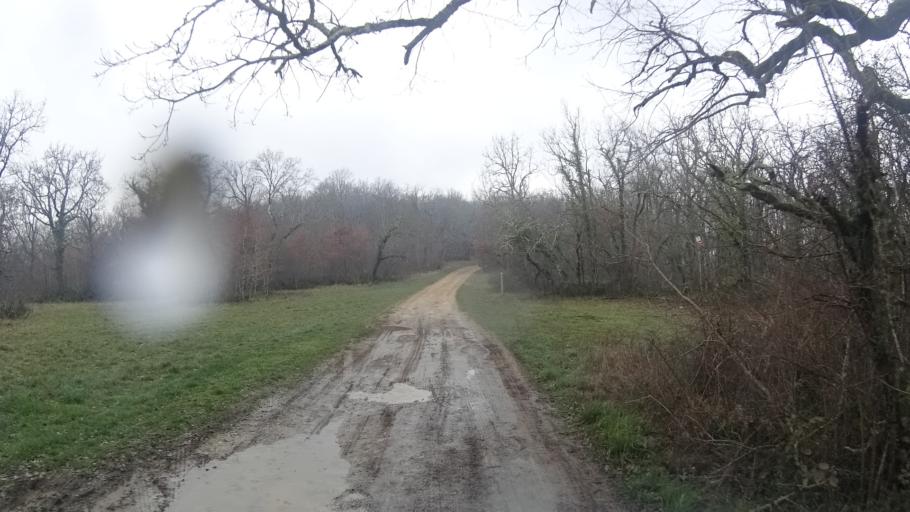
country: FR
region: Aquitaine
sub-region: Departement de la Dordogne
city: Montignac
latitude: 45.0879
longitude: 1.2176
